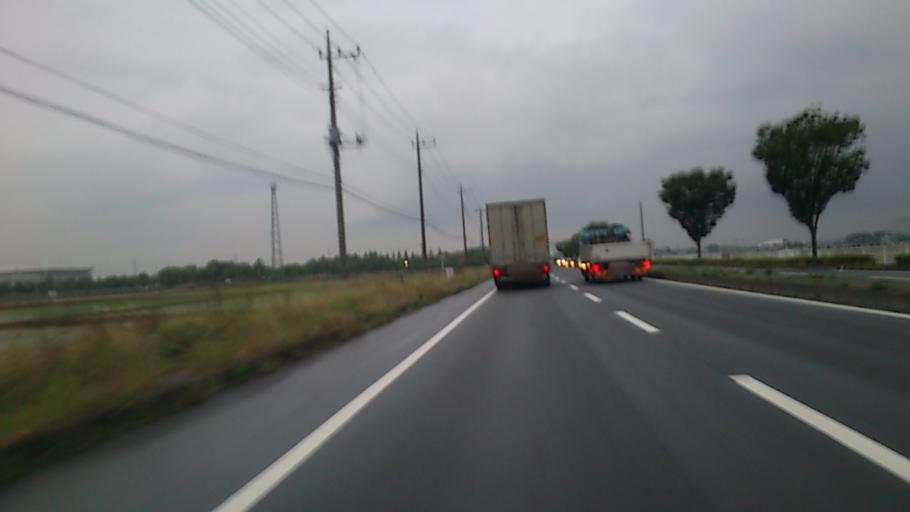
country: JP
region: Saitama
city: Gyoda
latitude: 36.1567
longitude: 139.4594
